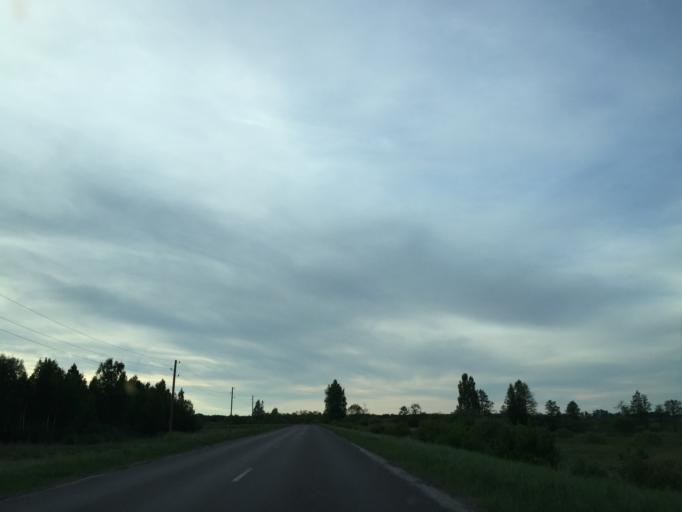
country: LV
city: Tireli
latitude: 56.8242
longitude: 23.5689
